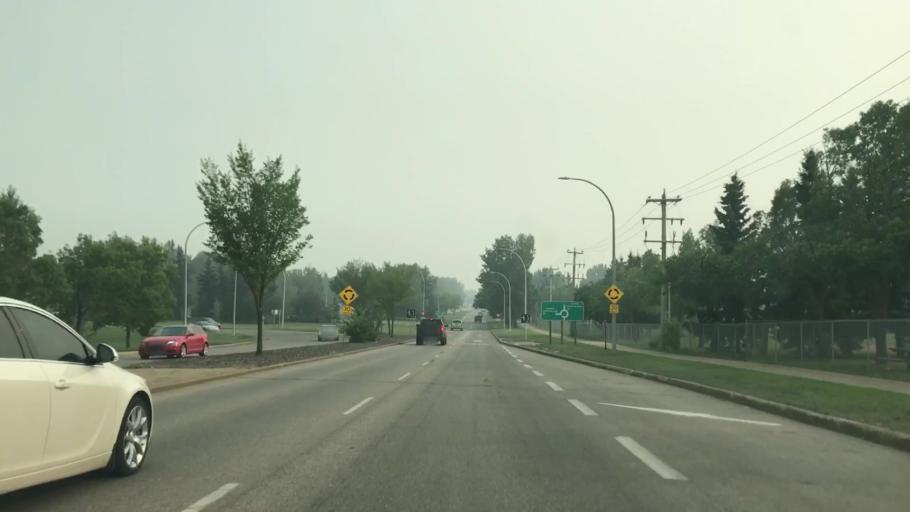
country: CA
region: Alberta
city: Sherwood Park
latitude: 53.5204
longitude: -113.3201
